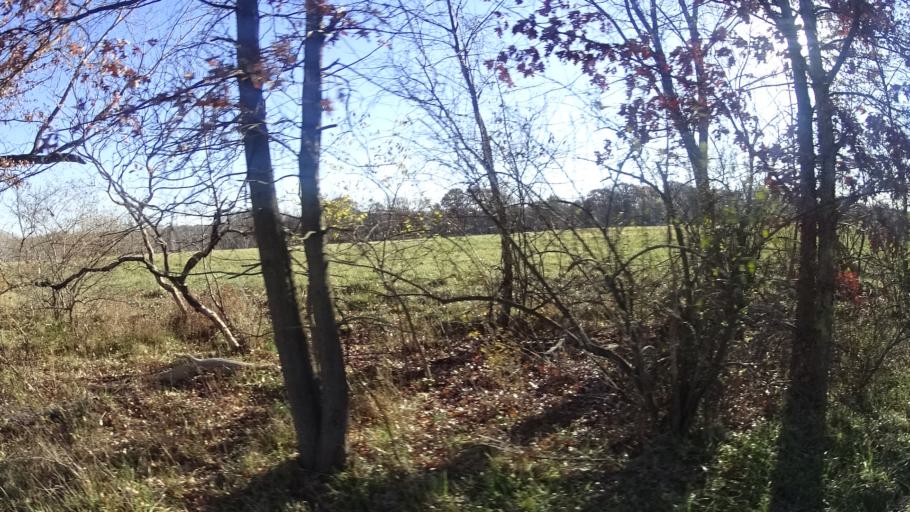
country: US
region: Ohio
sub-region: Lorain County
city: Sheffield
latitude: 41.4044
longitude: -82.0971
